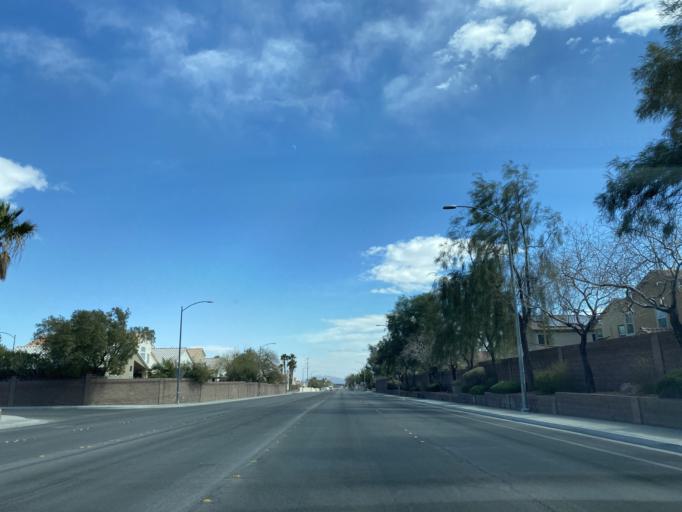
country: US
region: Nevada
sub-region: Clark County
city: Summerlin South
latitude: 36.2261
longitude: -115.2768
